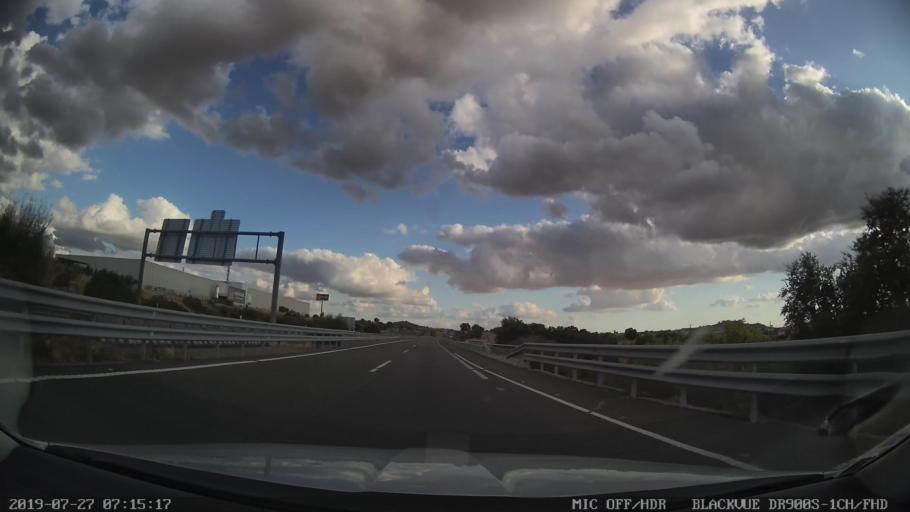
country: ES
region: Extremadura
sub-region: Provincia de Caceres
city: Trujillo
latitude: 39.4785
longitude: -5.8522
